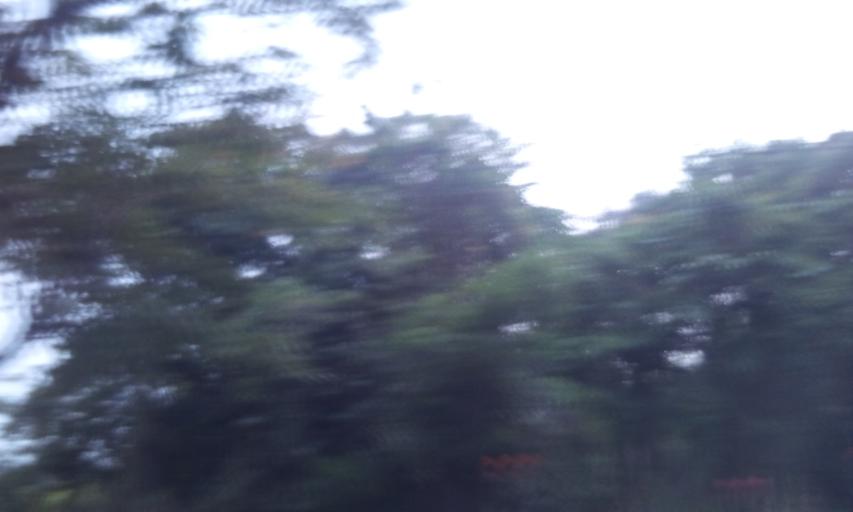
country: TH
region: Bangkok
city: Nong Chok
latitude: 13.8464
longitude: 100.8940
